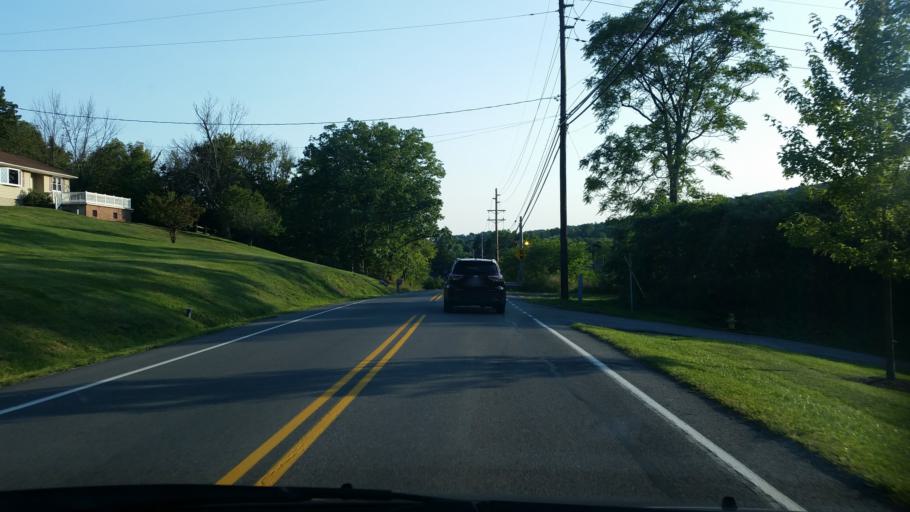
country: US
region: Pennsylvania
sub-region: Blair County
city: Altoona
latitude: 40.5420
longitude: -78.4005
